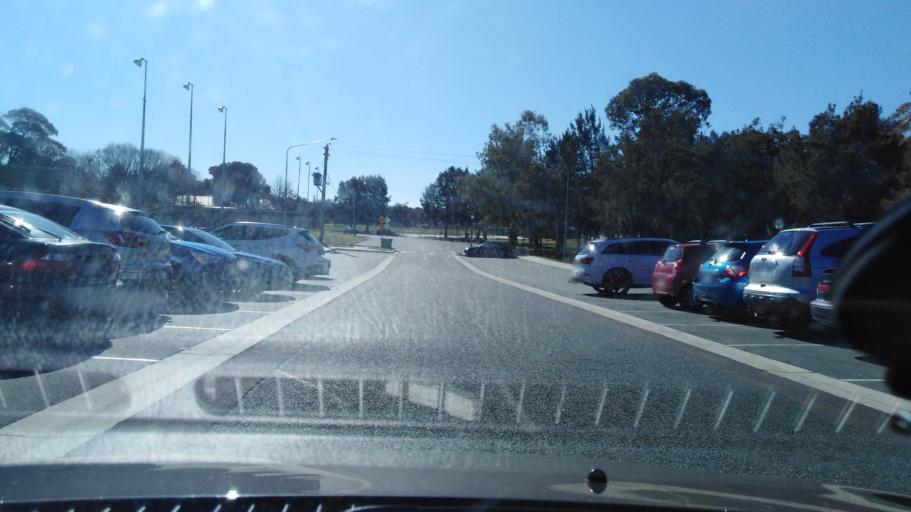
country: AU
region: Australian Capital Territory
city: Forrest
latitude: -35.3390
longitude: 149.0535
